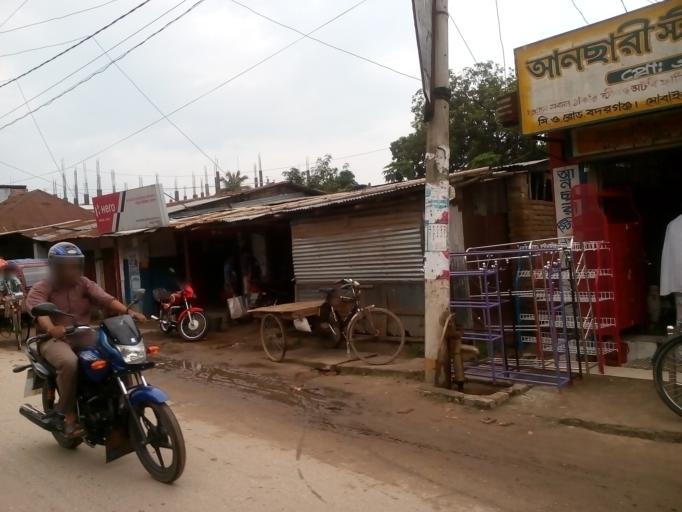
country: BD
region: Rangpur Division
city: Badarganj
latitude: 25.6712
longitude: 89.0544
